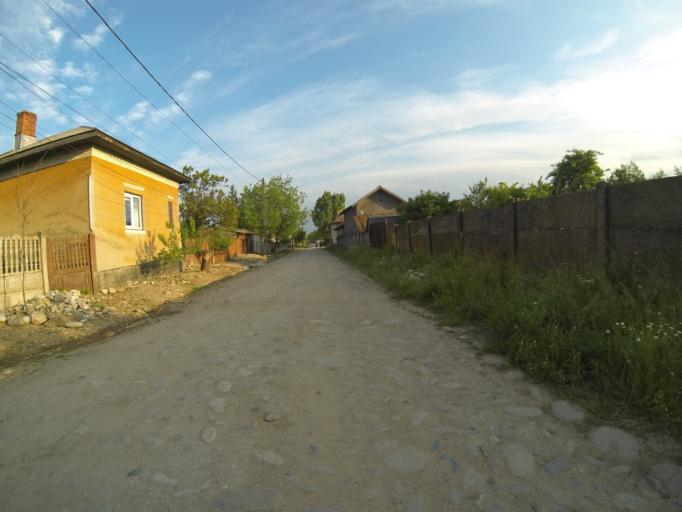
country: RO
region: Dolj
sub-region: Comuna Segarcea
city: Segarcea
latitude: 44.0956
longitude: 23.7489
